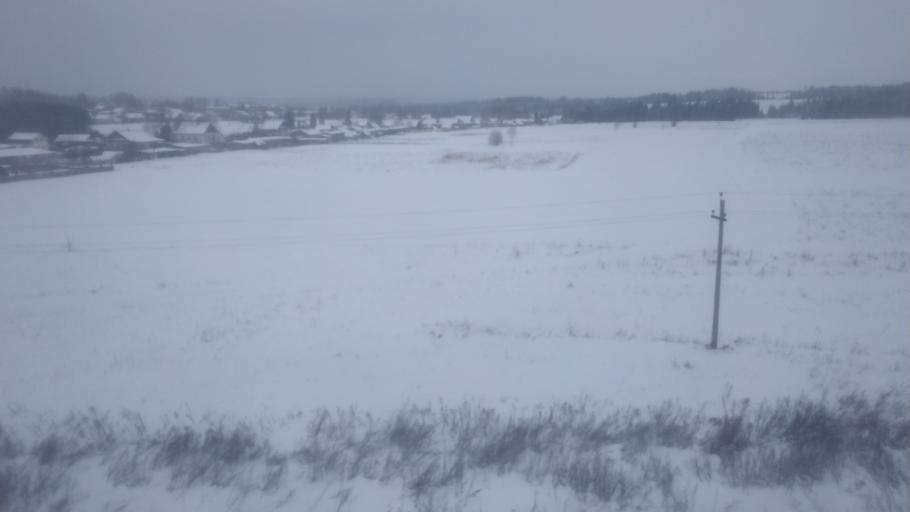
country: RU
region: Udmurtiya
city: Kiyasovo
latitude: 56.5025
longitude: 53.2242
